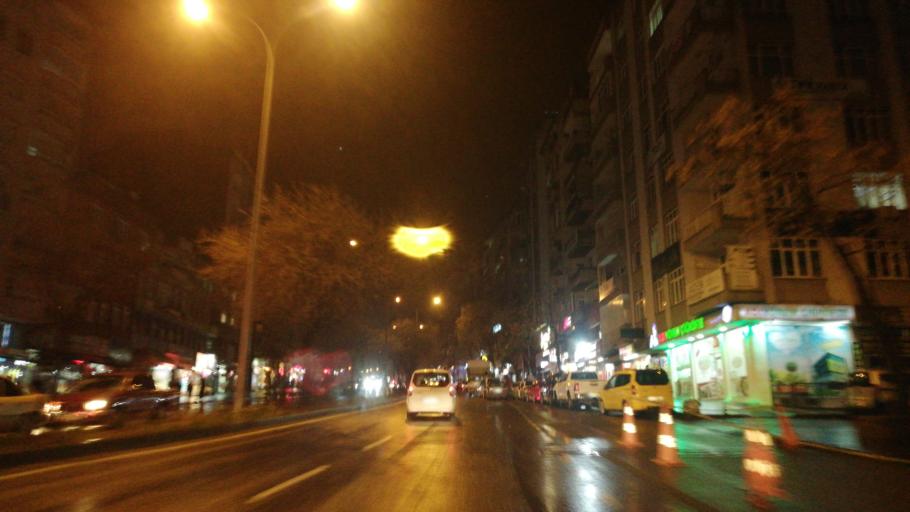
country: TR
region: Kahramanmaras
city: Kahramanmaras
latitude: 37.5774
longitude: 36.9270
